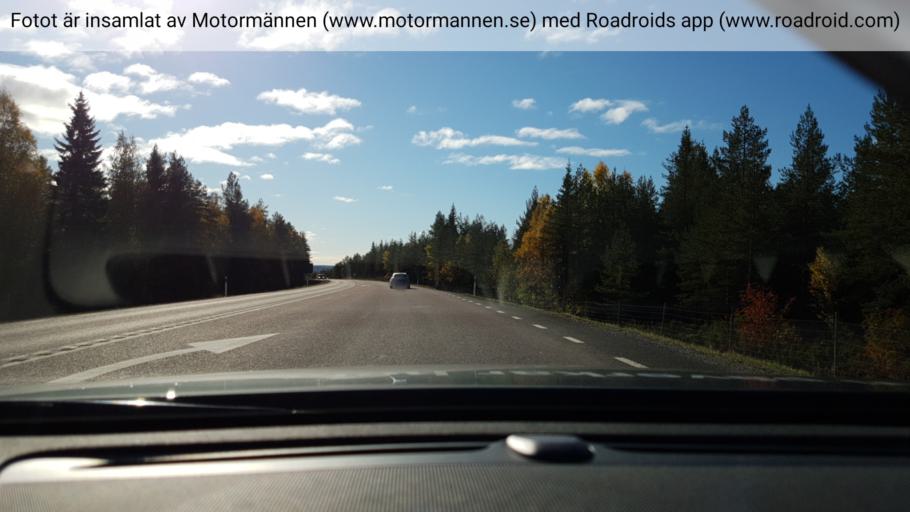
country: SE
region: Vaesterbotten
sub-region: Skelleftea Kommun
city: Burea
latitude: 64.4346
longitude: 21.2799
